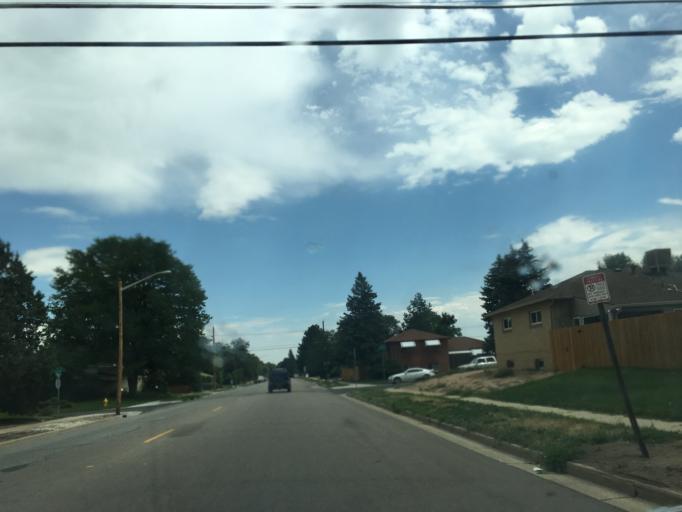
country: US
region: Colorado
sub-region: Jefferson County
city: Lakewood
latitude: 39.6791
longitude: -105.0507
